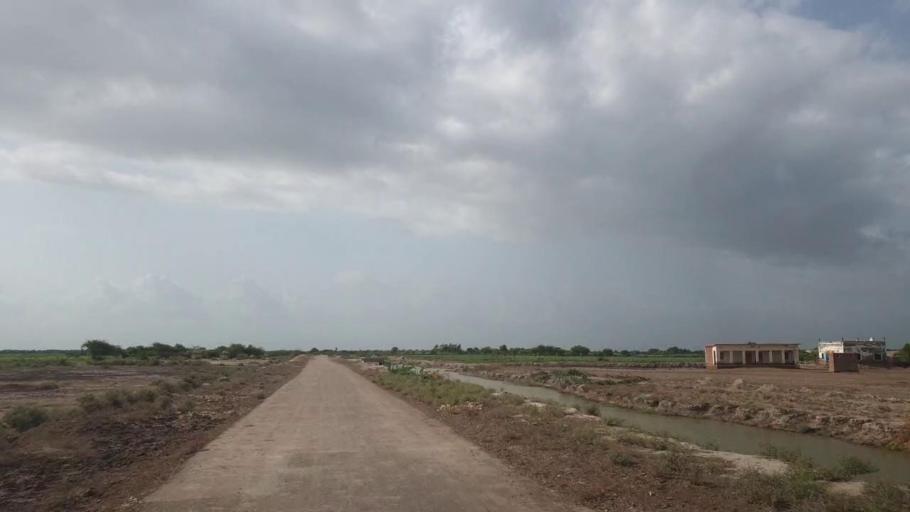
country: PK
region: Sindh
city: Kadhan
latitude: 24.5692
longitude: 69.0622
